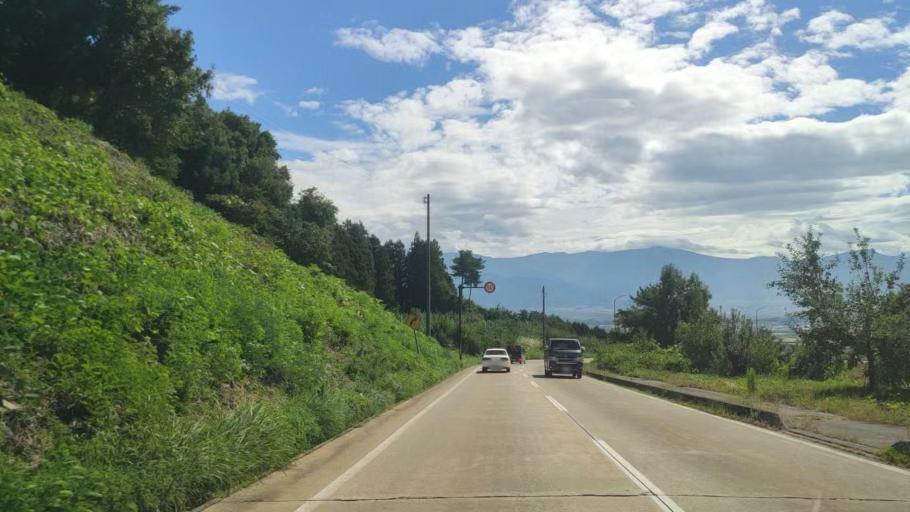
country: JP
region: Nagano
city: Suzaka
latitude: 36.7113
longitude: 138.2501
